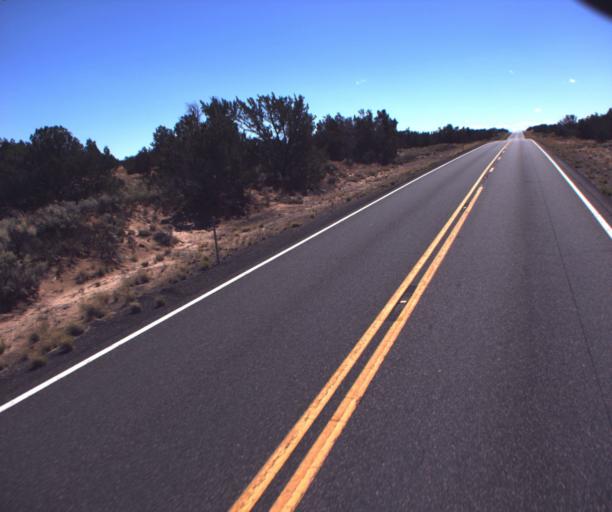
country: US
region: Arizona
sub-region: Apache County
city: Saint Johns
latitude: 34.8476
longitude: -109.2377
